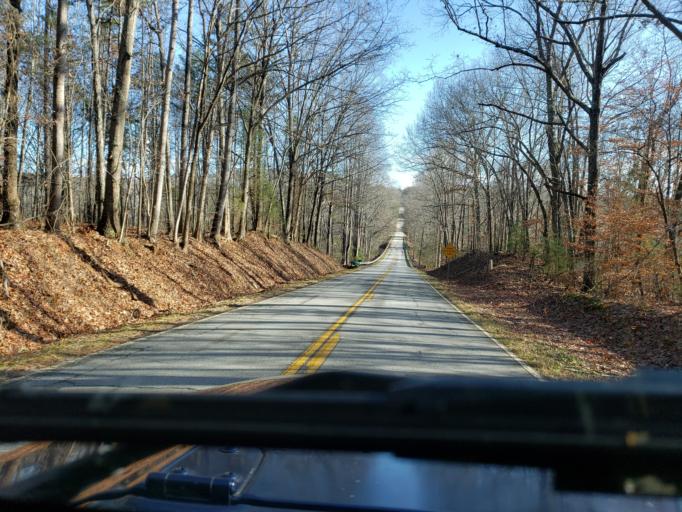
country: US
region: North Carolina
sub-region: Cleveland County
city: White Plains
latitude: 35.1580
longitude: -81.4030
